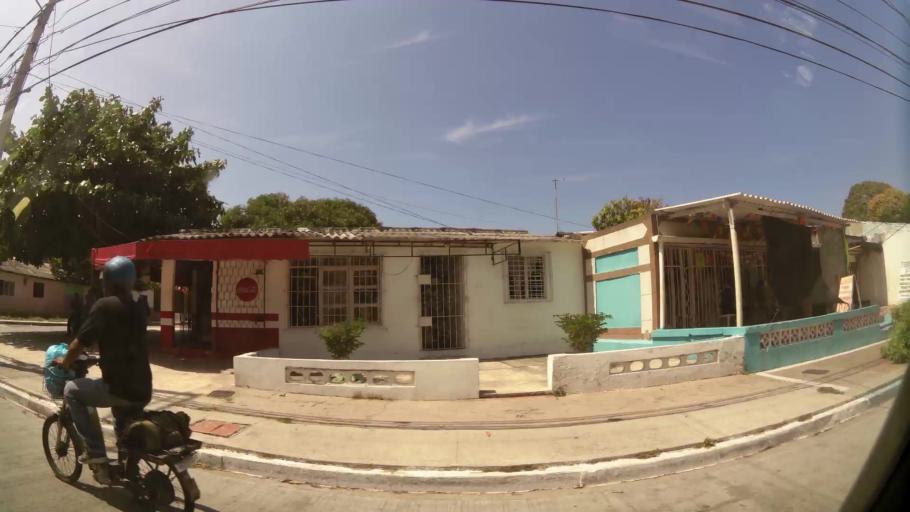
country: CO
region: Atlantico
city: Barranquilla
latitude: 10.9666
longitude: -74.8062
